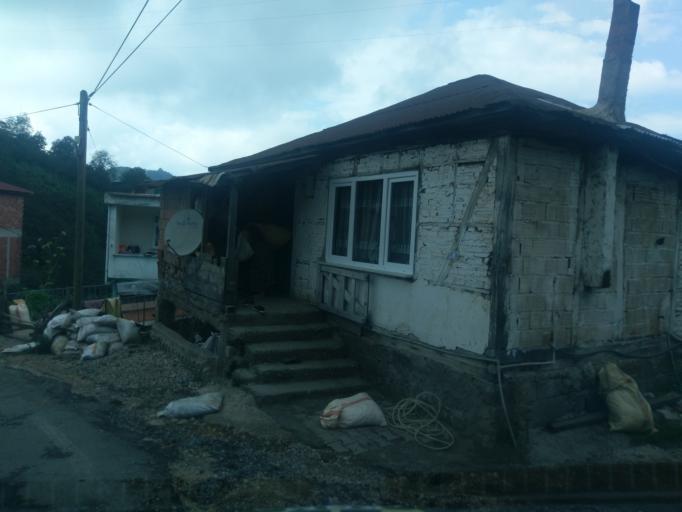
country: TR
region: Ordu
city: Camas
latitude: 40.8911
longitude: 37.6251
